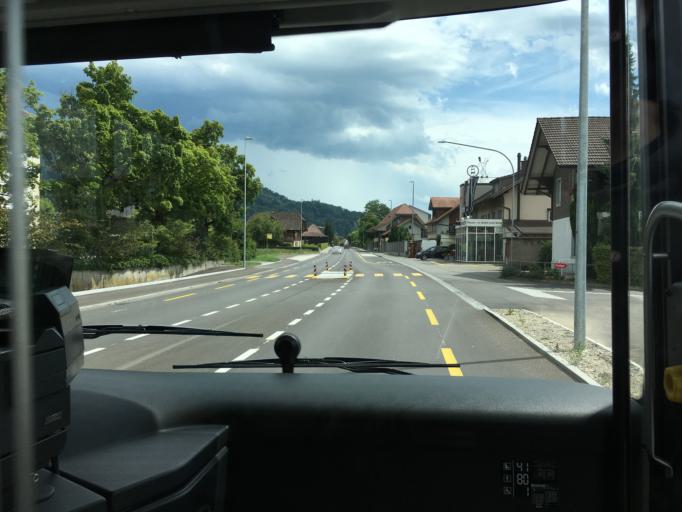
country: CH
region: Bern
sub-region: Thun District
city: Steffisburg
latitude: 46.7695
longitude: 7.6196
